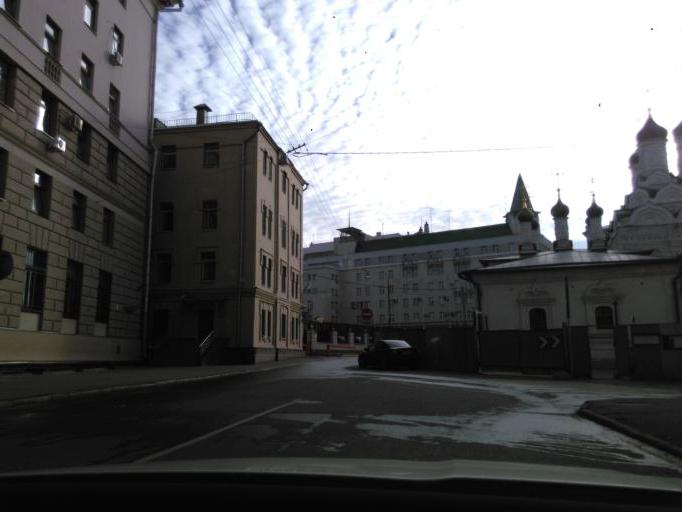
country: RU
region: Moscow
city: Moscow
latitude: 55.7693
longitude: 37.6134
